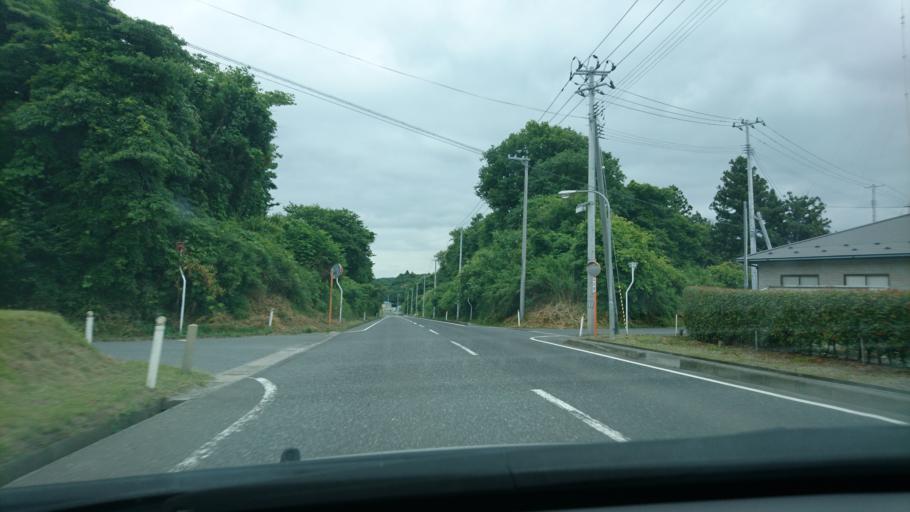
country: JP
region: Miyagi
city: Kogota
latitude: 38.7271
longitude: 141.0492
